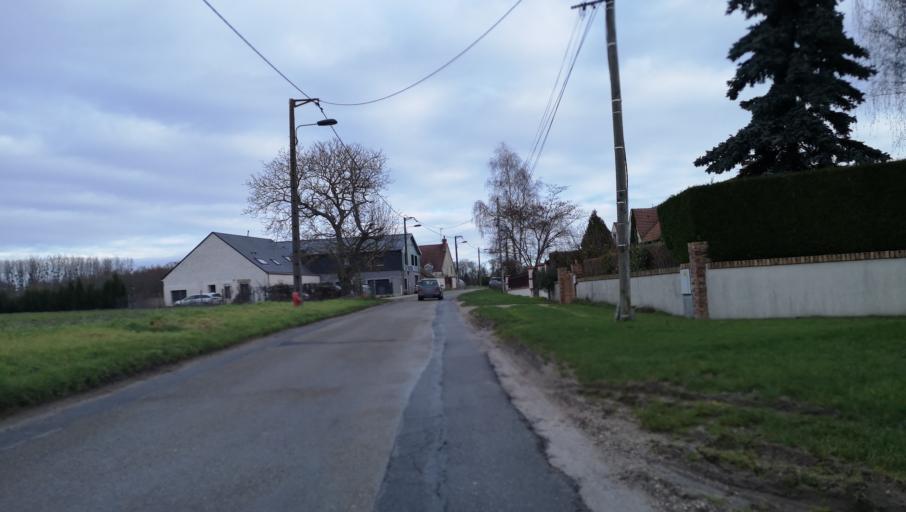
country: FR
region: Centre
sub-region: Departement du Loiret
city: Boigny-sur-Bionne
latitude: 47.9131
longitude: 2.0037
